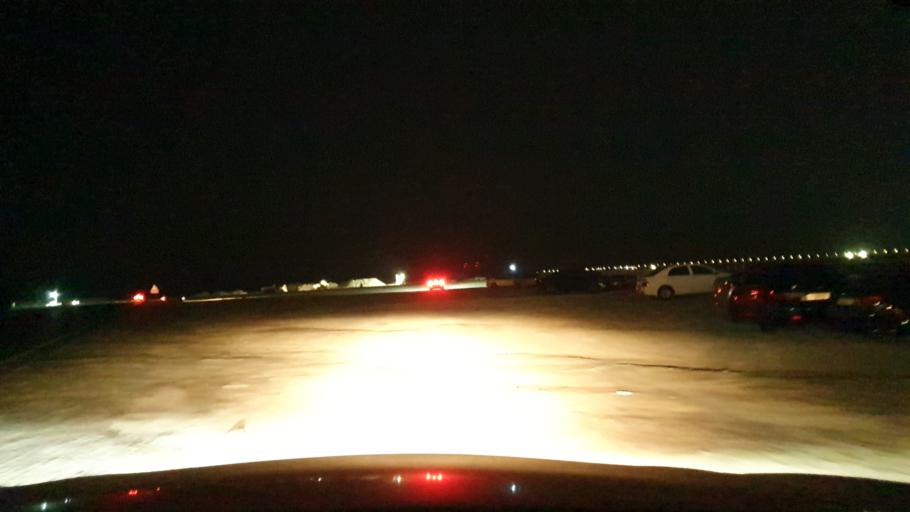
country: BH
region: Muharraq
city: Al Muharraq
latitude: 26.2540
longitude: 50.5845
